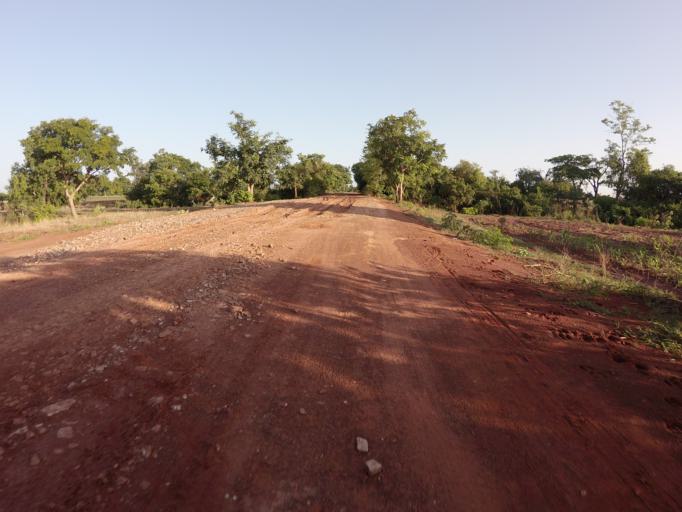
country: TG
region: Savanes
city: Sansanne-Mango
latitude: 10.3478
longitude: -0.0928
